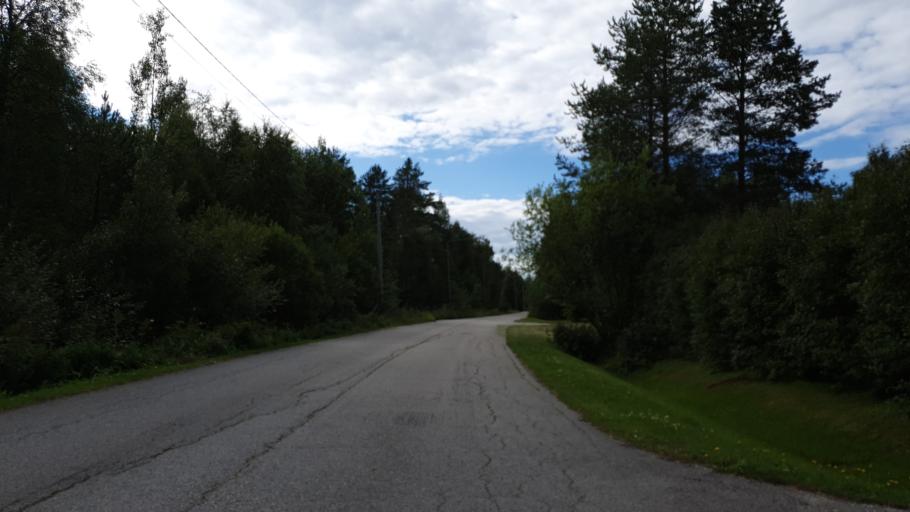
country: FI
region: Kainuu
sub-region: Kehys-Kainuu
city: Kuhmo
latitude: 64.1185
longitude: 29.5642
